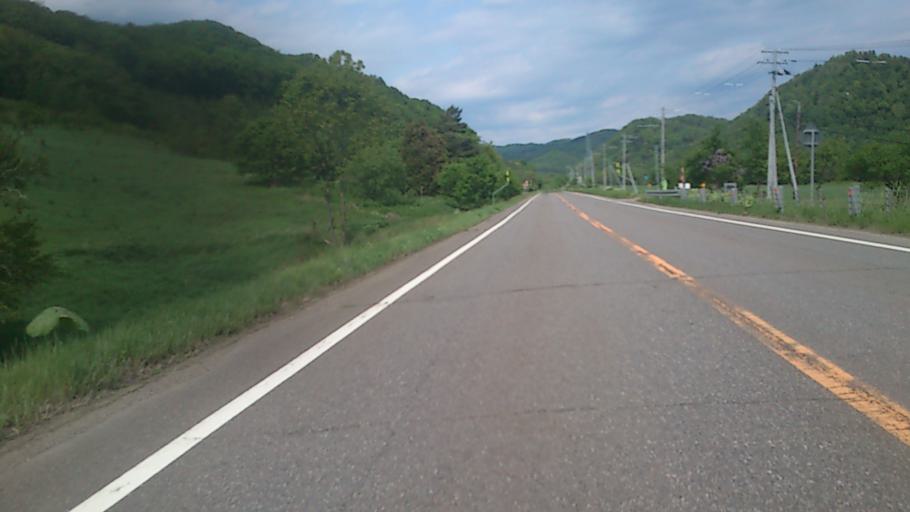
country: JP
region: Hokkaido
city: Kitami
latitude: 43.3442
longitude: 143.7689
